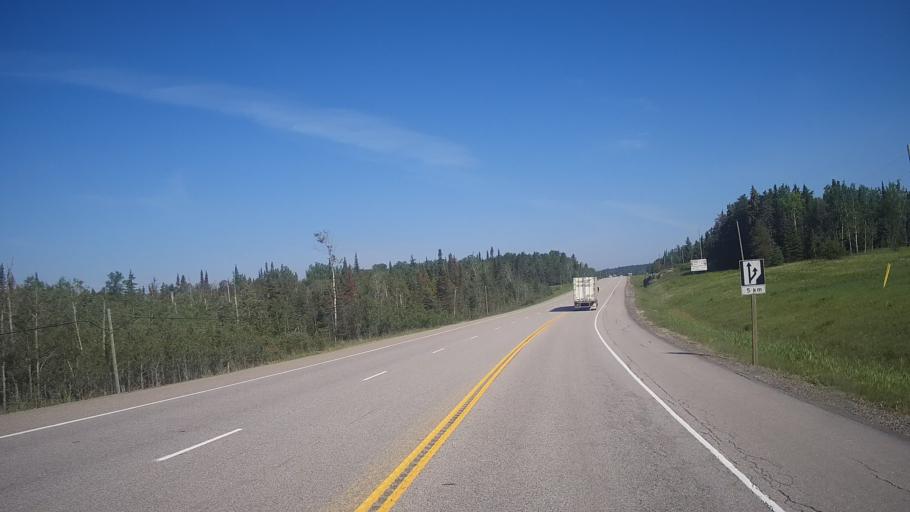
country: CA
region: Ontario
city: Dryden
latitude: 49.7070
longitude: -92.5849
